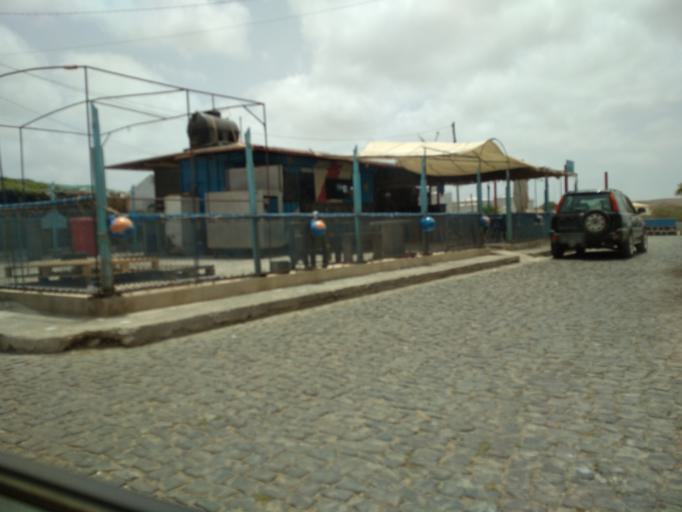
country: CV
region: Sal
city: Espargos
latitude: 16.7571
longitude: -22.9806
